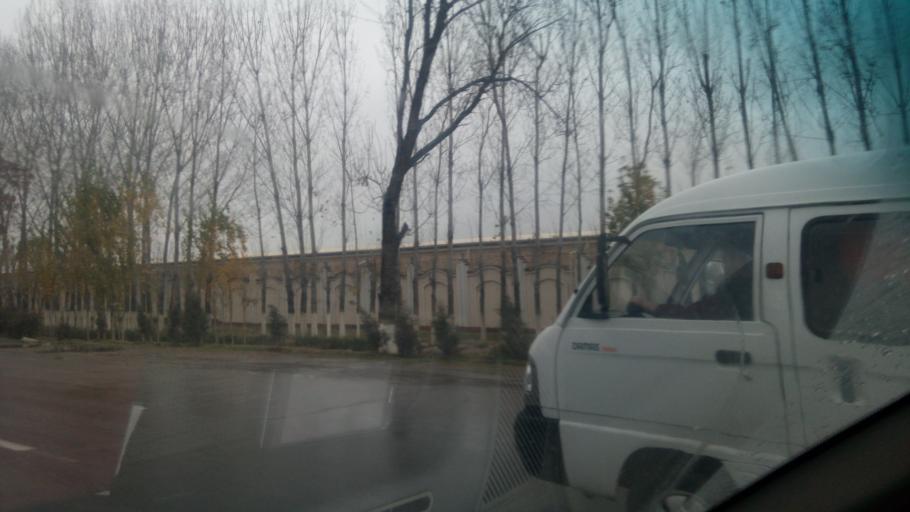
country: UZ
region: Toshkent
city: Urtaowul
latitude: 41.2273
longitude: 69.1467
